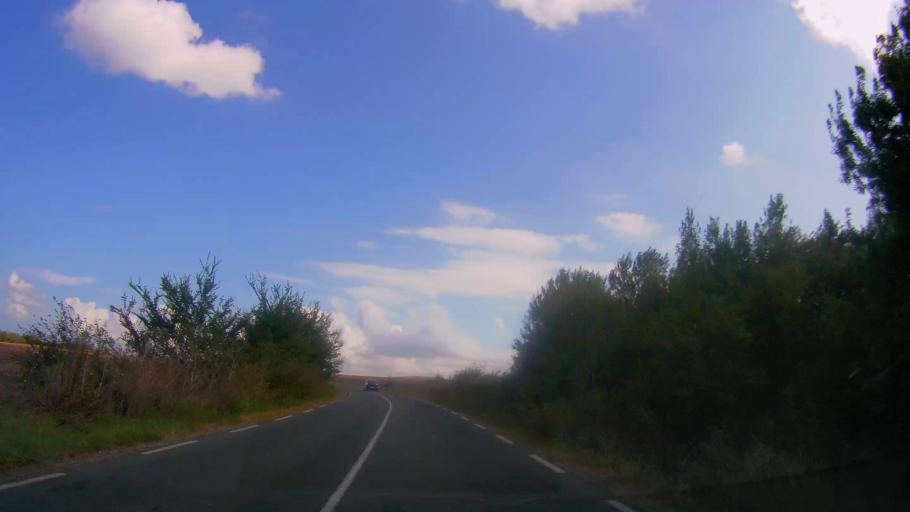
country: BG
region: Burgas
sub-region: Obshtina Kameno
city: Kameno
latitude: 42.4790
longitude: 27.3480
